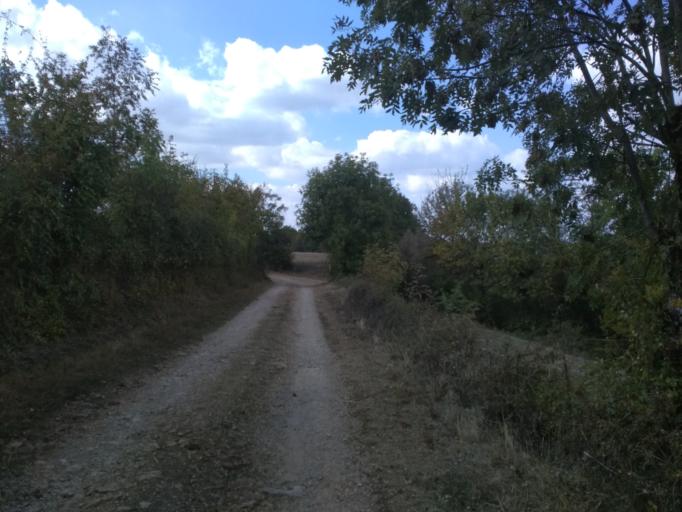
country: FR
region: Midi-Pyrenees
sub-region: Departement de l'Aveyron
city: Bozouls
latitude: 44.4762
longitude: 2.6715
